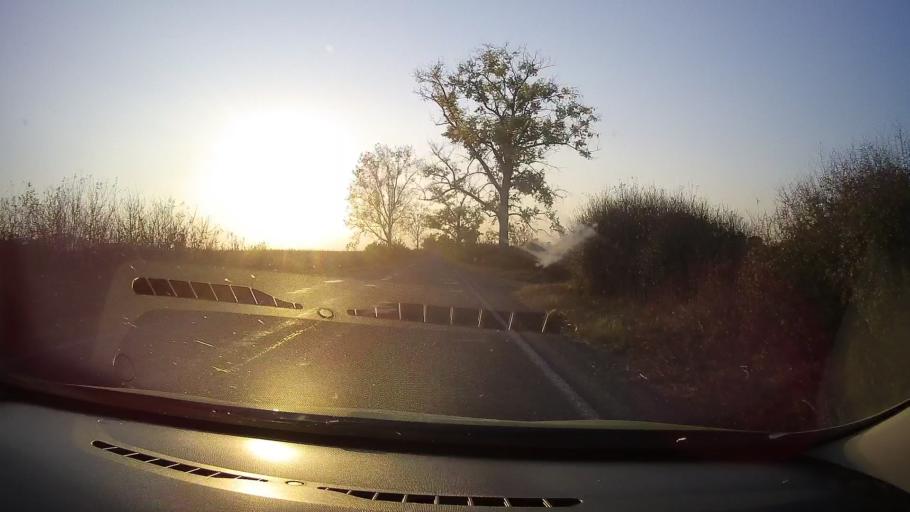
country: RO
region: Arad
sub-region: Comuna Bocsig
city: Bocsig
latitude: 46.4290
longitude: 21.9017
